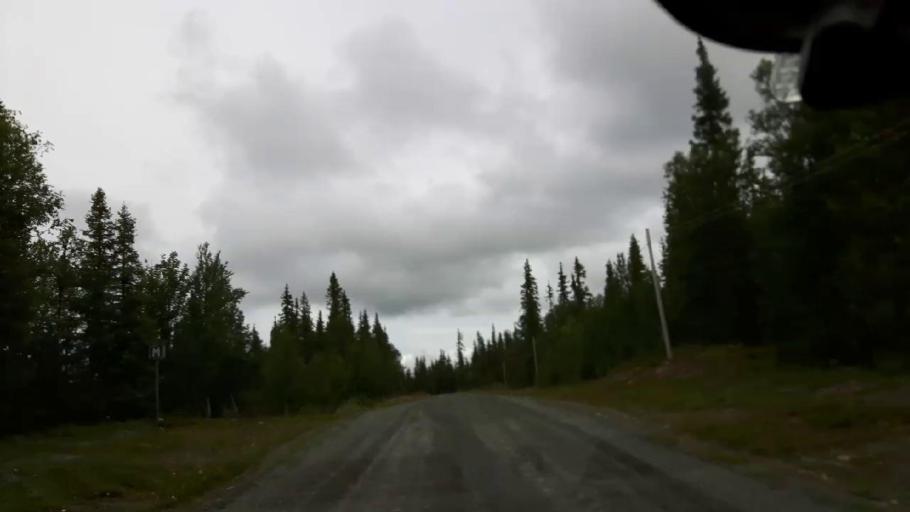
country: SE
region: Jaemtland
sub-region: Krokoms Kommun
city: Valla
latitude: 63.7618
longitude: 13.8370
